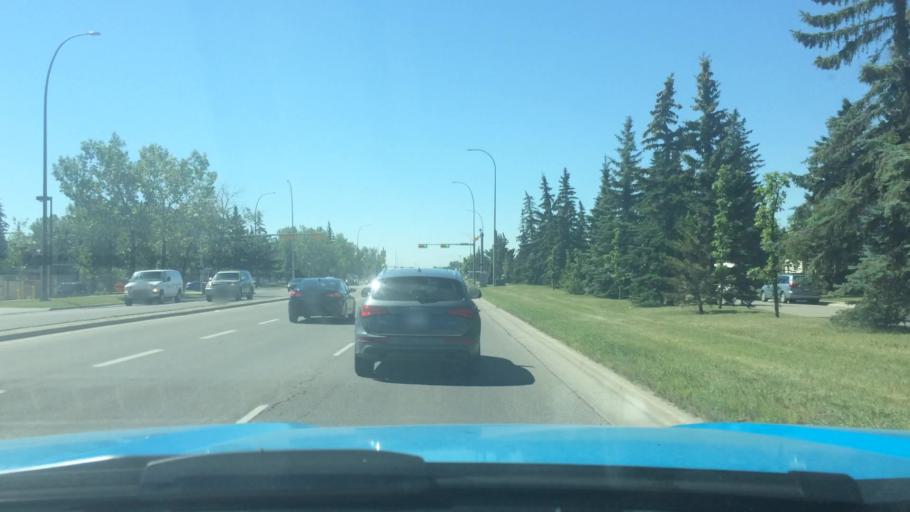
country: CA
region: Alberta
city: Calgary
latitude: 51.0750
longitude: -113.9585
